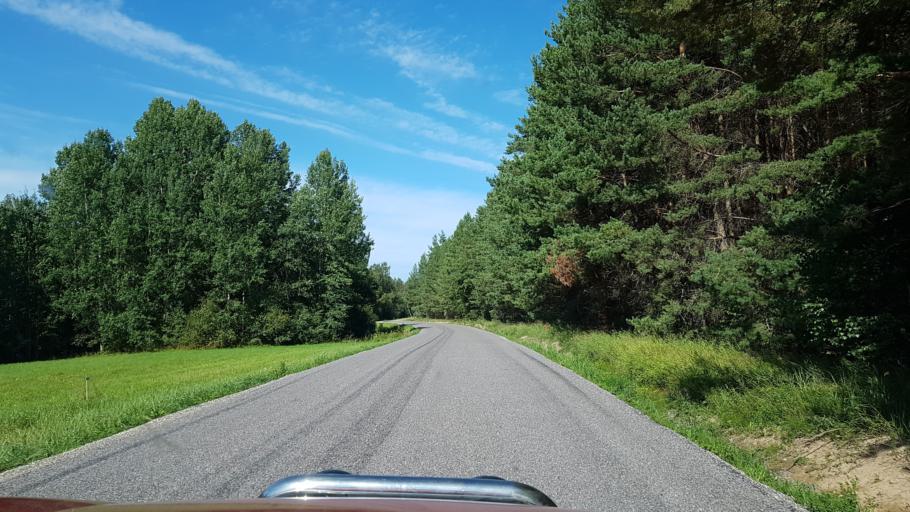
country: EE
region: Tartu
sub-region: Elva linn
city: Elva
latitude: 58.2485
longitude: 26.3768
